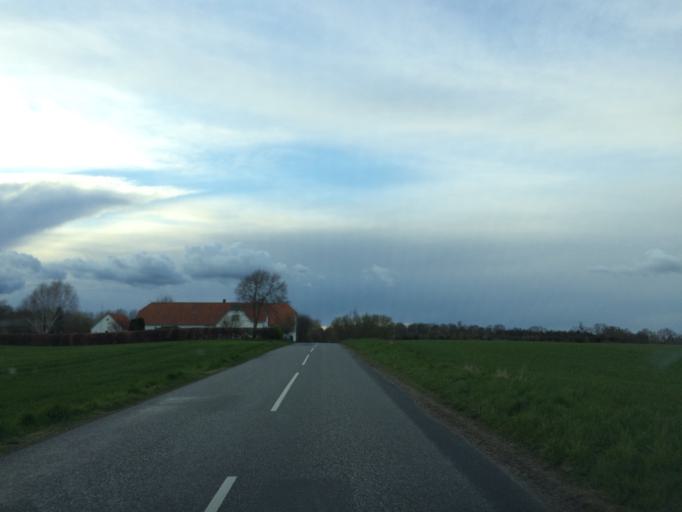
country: DK
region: South Denmark
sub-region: Odense Kommune
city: Bellinge
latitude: 55.2831
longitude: 10.2979
